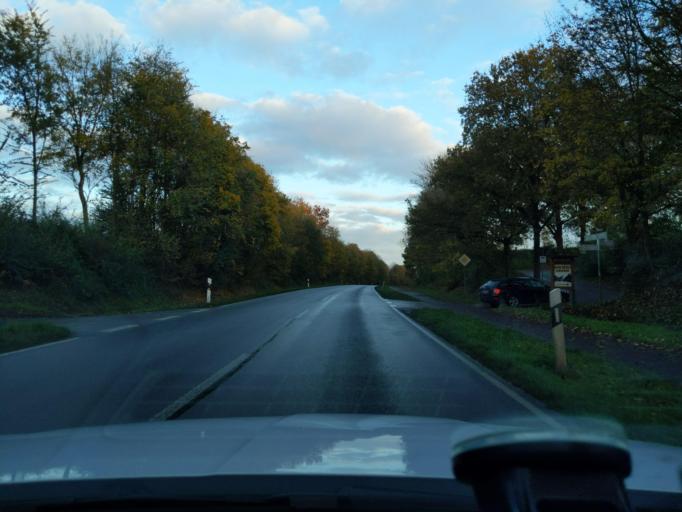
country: DE
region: North Rhine-Westphalia
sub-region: Regierungsbezirk Dusseldorf
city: Uedem
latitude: 51.6718
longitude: 6.2891
